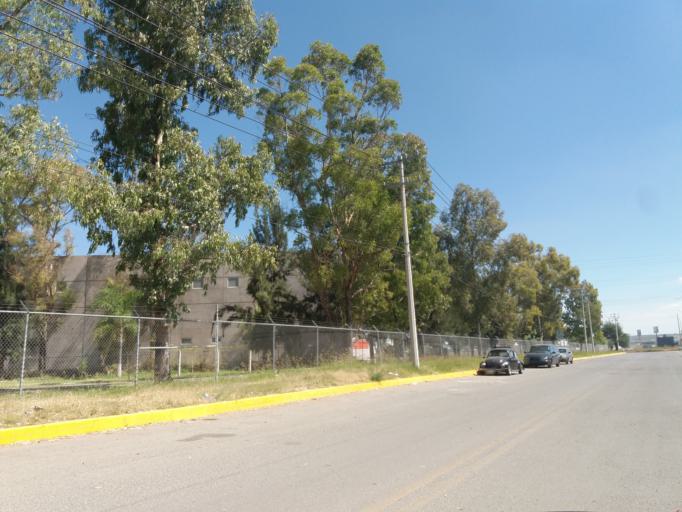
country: MX
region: Aguascalientes
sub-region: Aguascalientes
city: San Sebastian [Fraccionamiento]
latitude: 21.7987
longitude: -102.2908
